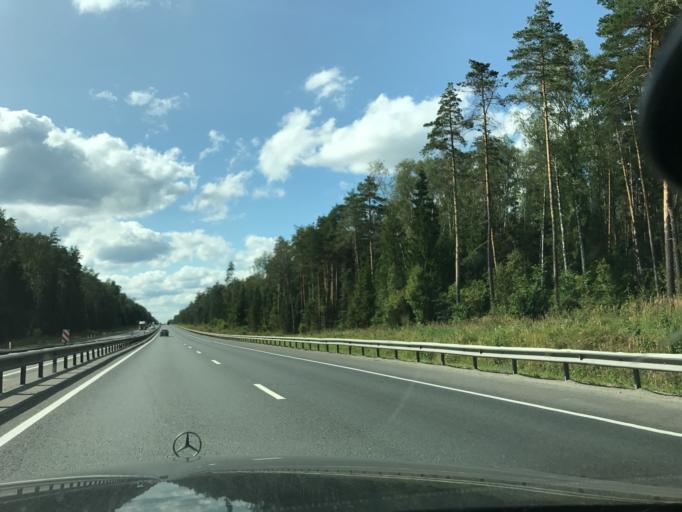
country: RU
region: Vladimir
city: Krasnyy Oktyabr'
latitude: 56.2158
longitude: 41.4043
